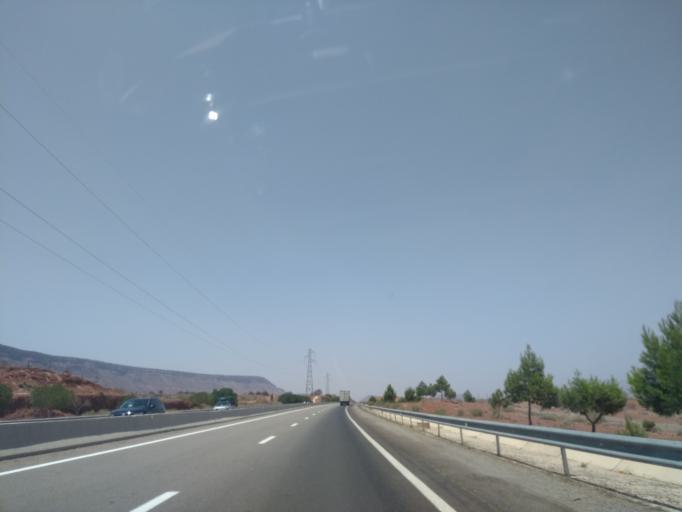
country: MA
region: Marrakech-Tensift-Al Haouz
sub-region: Chichaoua
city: Timezgadiouine
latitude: 30.8900
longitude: -9.0774
